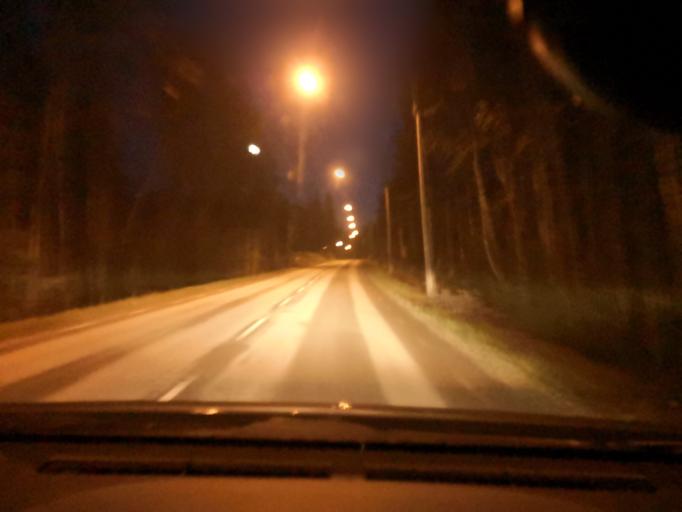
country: SE
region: OErebro
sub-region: Orebro Kommun
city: Orebro
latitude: 59.2506
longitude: 15.2793
